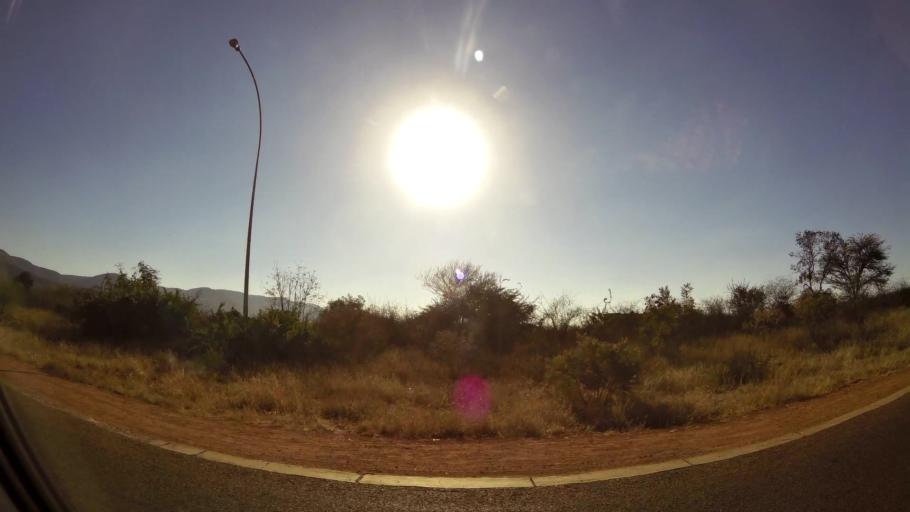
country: ZA
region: Limpopo
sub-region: Waterberg District Municipality
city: Mokopane
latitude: -24.2041
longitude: 29.0004
